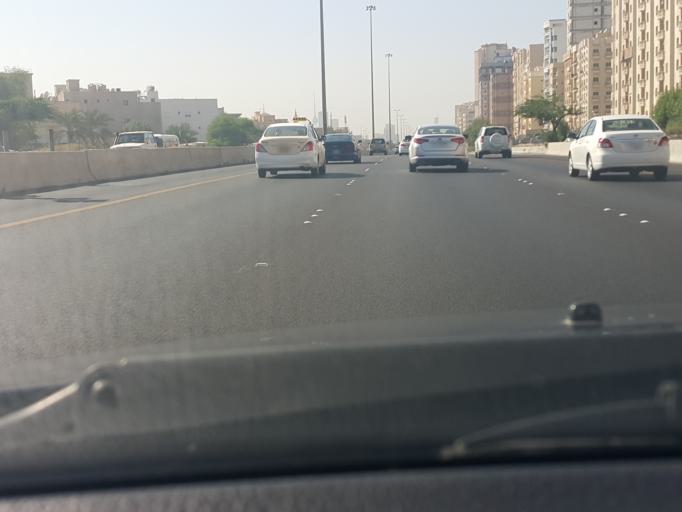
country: KW
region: Muhafazat Hawalli
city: Hawalli
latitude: 29.3253
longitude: 48.0105
